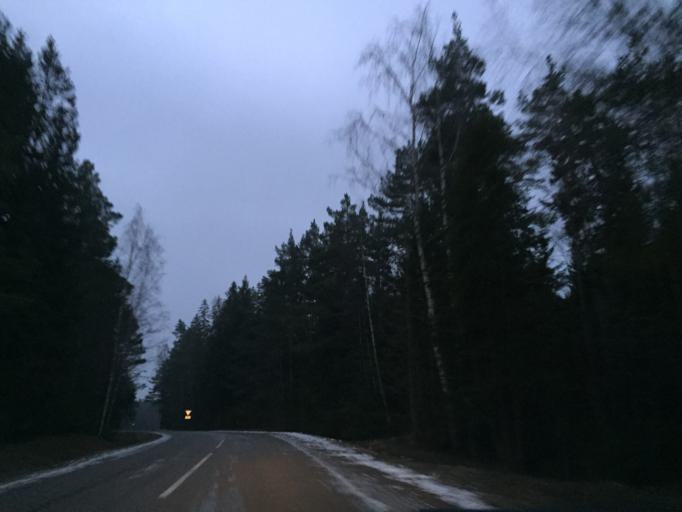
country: EE
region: Saare
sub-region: Kuressaare linn
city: Kuressaare
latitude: 58.5935
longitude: 22.6071
